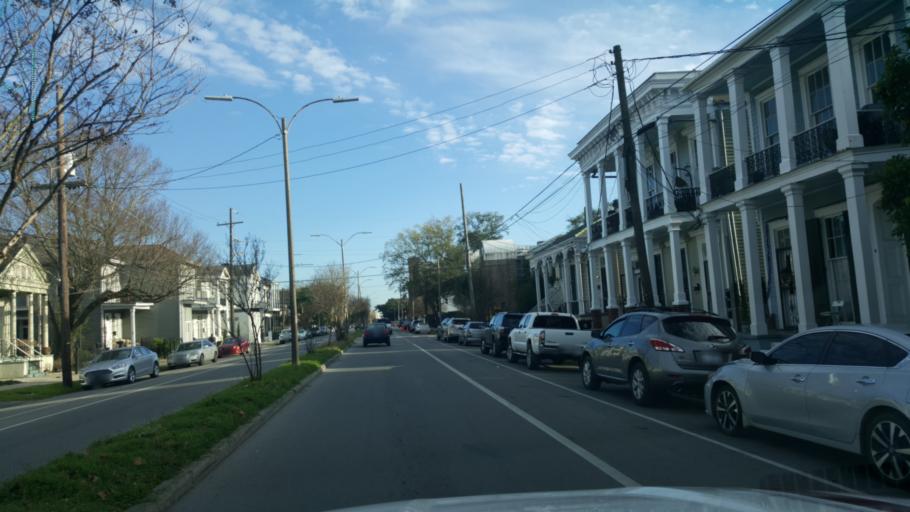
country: US
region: Louisiana
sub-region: Jefferson Parish
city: Harvey
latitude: 29.9285
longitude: -90.0759
